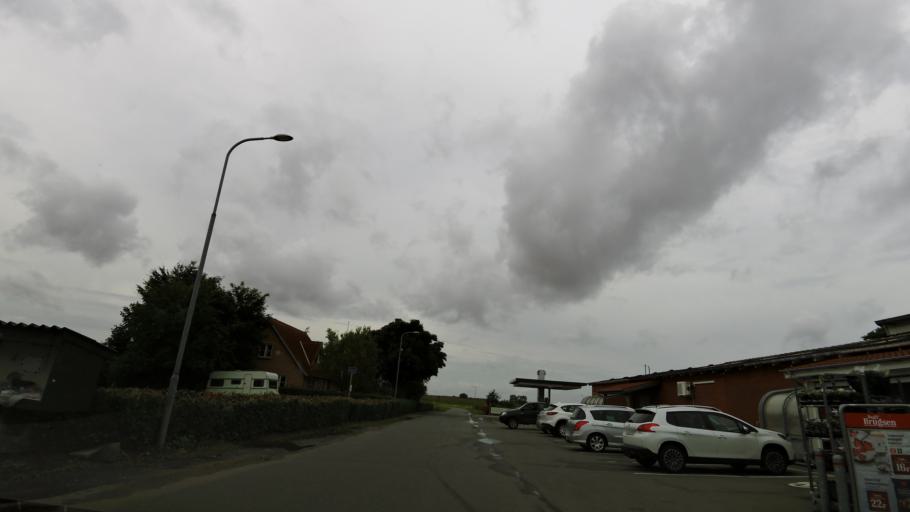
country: DK
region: South Denmark
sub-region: Nordfyns Kommune
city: Otterup
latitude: 55.5742
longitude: 10.3940
